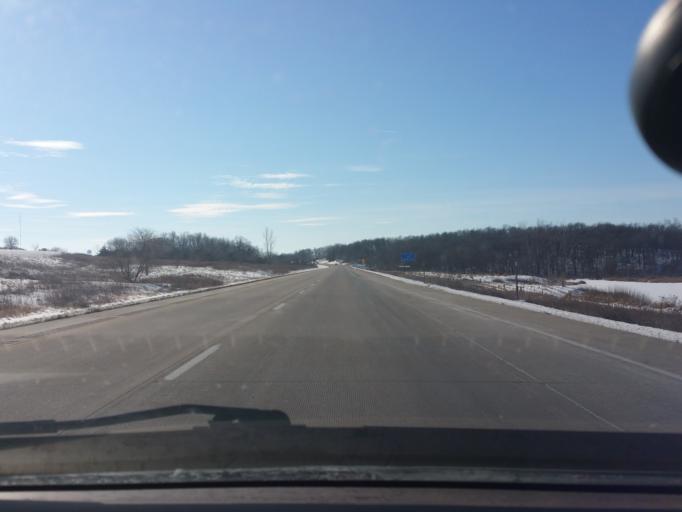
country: US
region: Iowa
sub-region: Clarke County
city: Osceola
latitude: 41.0074
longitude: -93.7983
